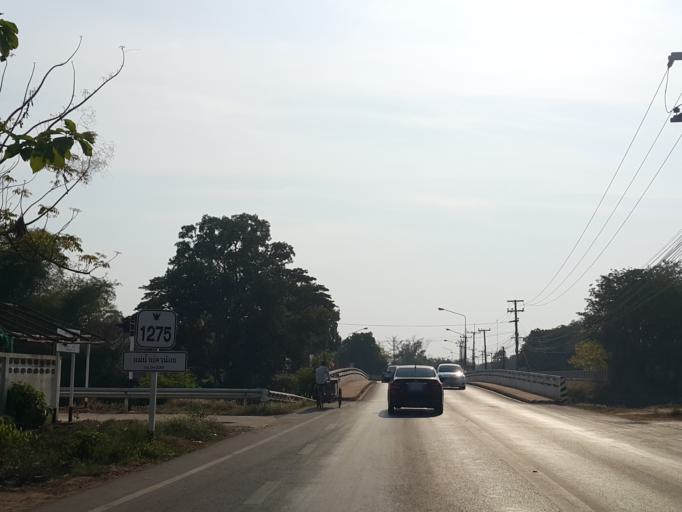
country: TH
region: Phitsanulok
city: Phrom Phiram
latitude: 16.9387
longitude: 100.2279
